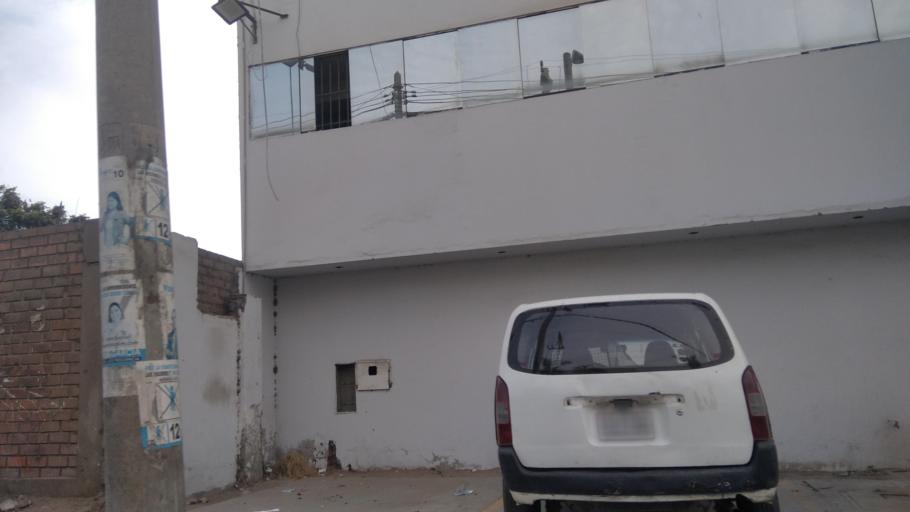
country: PE
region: Lima
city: Lima
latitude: -12.0191
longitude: -76.9984
